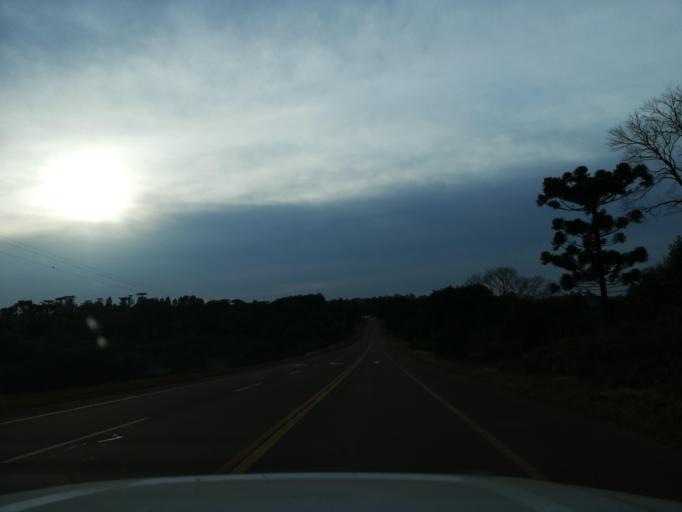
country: AR
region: Misiones
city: San Vicente
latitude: -26.6371
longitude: -54.1355
